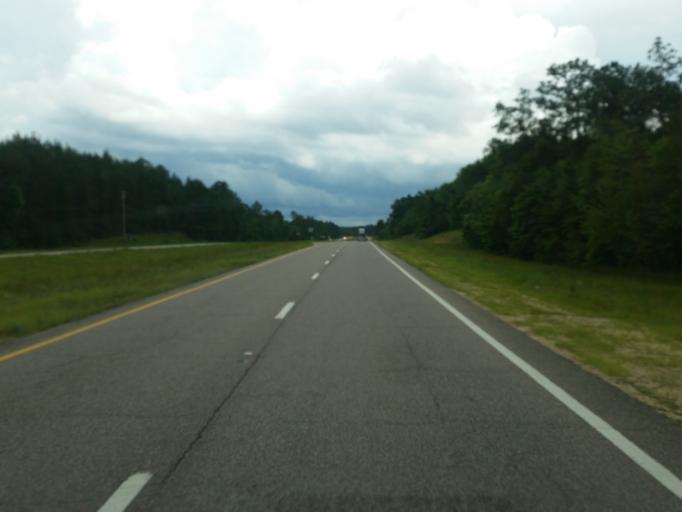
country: US
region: Mississippi
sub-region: George County
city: Lucedale
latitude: 30.8751
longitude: -88.4324
